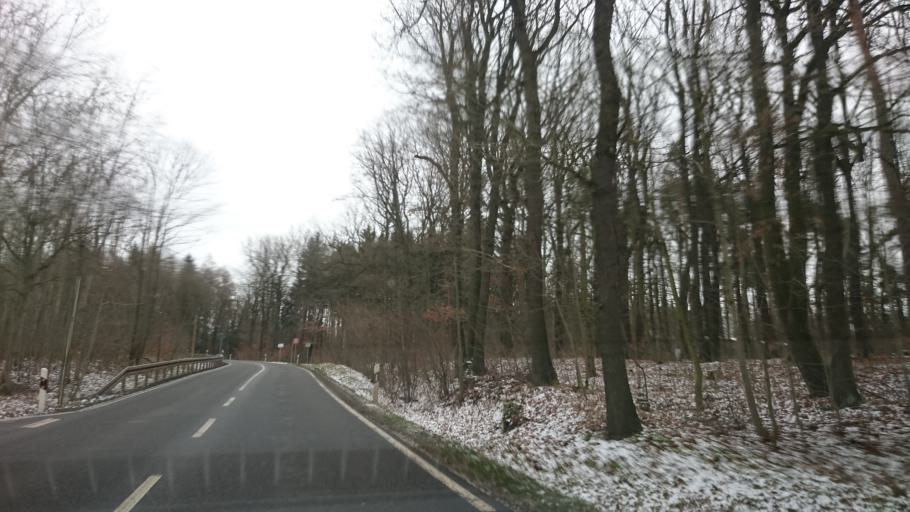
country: DE
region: Saxony
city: Hartmannsdorf
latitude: 50.7454
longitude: 12.4440
